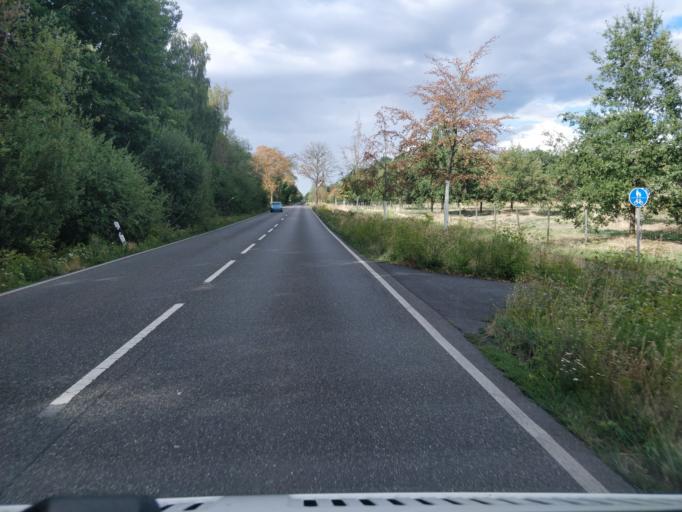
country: DE
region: North Rhine-Westphalia
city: Meckenheim
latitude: 50.6442
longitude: 7.0400
